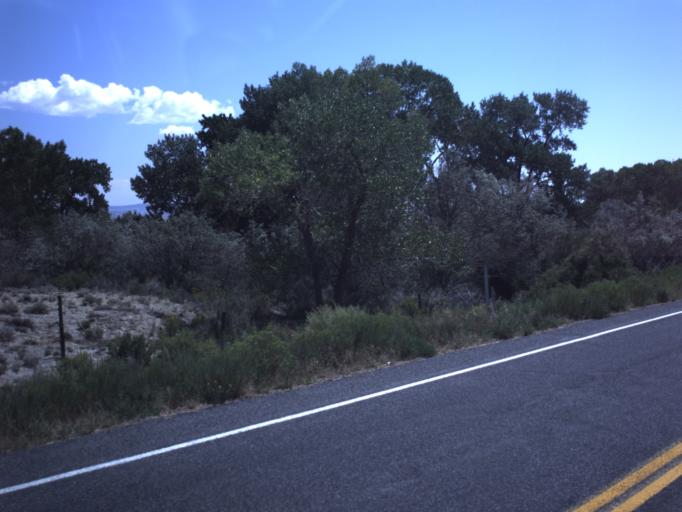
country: US
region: Utah
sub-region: Emery County
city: Orangeville
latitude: 39.2165
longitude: -111.0656
